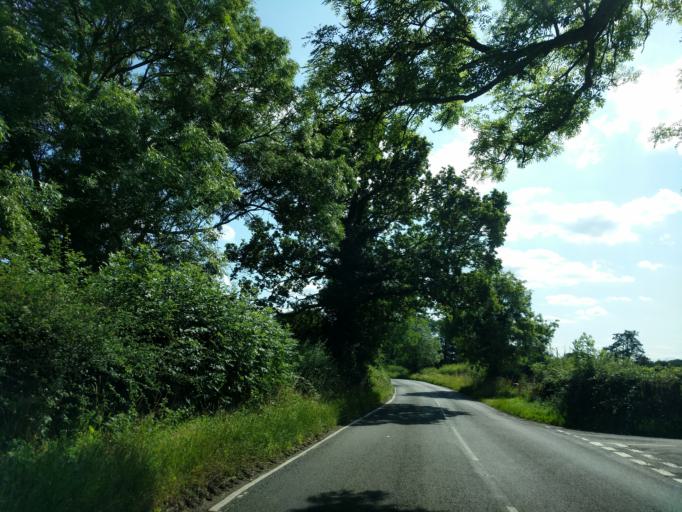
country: GB
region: England
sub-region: Staffordshire
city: Rugeley
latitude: 52.7904
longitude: -1.9352
